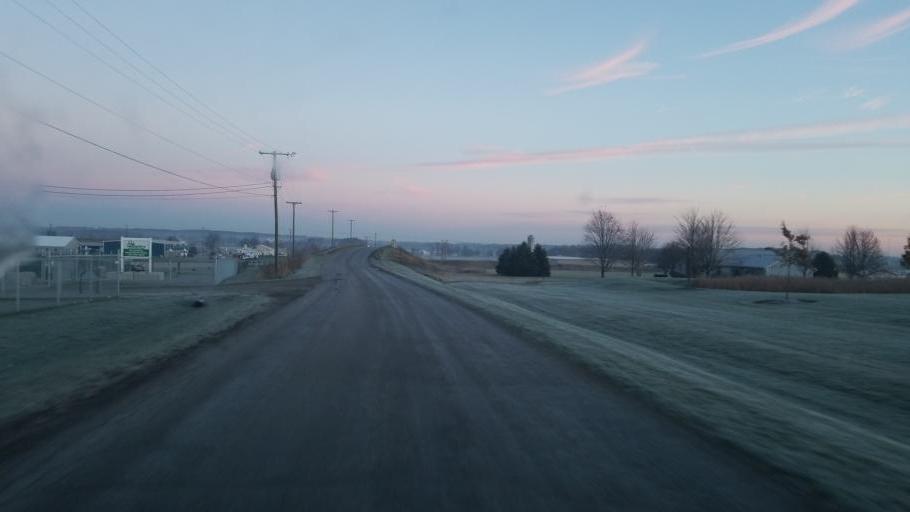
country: US
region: Ohio
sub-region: Wayne County
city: Orrville
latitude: 40.7938
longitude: -81.7774
